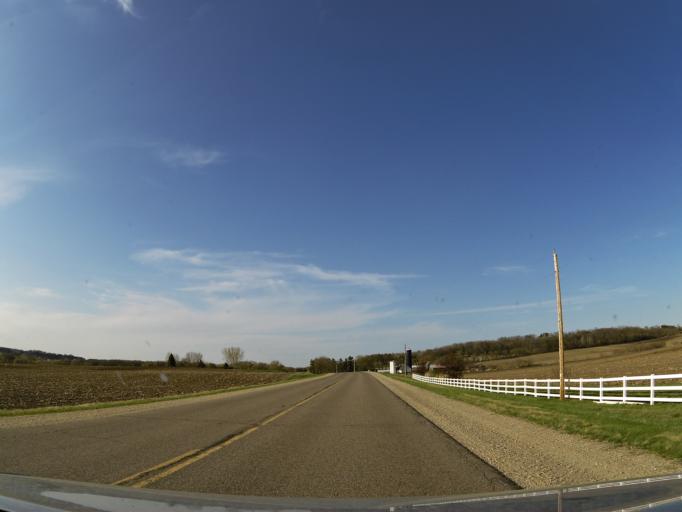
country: US
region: Wisconsin
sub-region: Pierce County
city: River Falls
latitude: 44.7984
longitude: -92.6452
